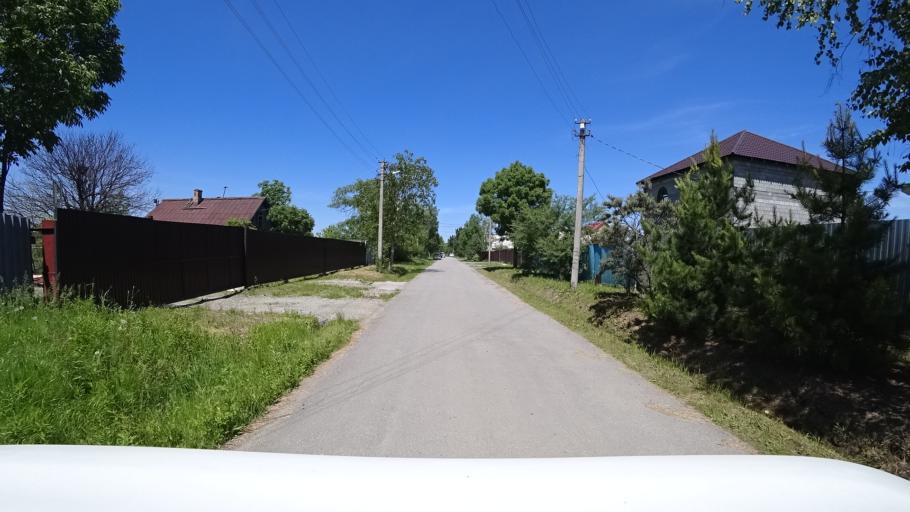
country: RU
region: Khabarovsk Krai
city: Topolevo
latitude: 48.5111
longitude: 135.1749
